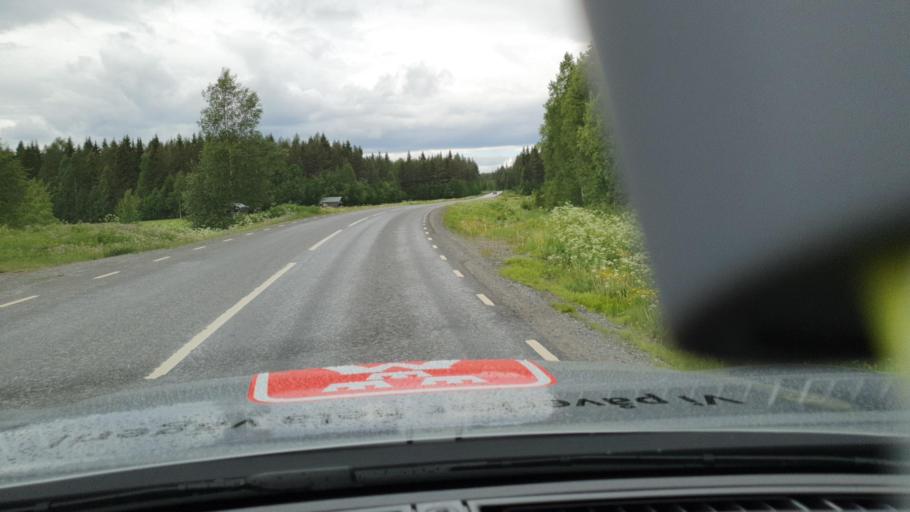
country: SE
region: Norrbotten
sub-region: Lulea Kommun
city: Ranea
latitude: 65.7843
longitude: 22.1625
